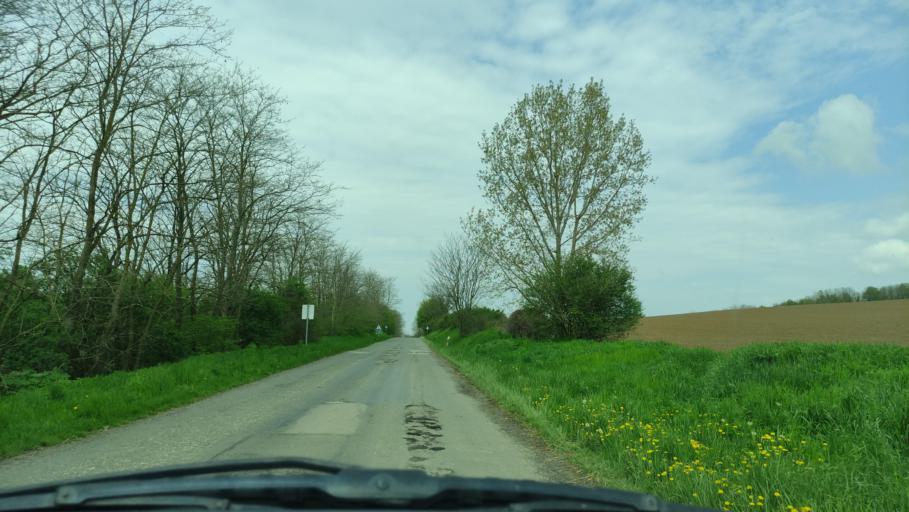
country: HU
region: Baranya
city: Magocs
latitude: 46.2986
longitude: 18.1754
